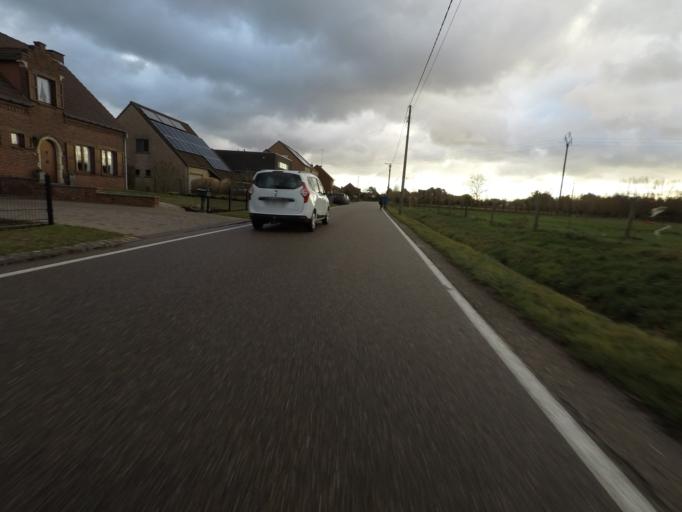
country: BE
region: Flanders
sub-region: Provincie Vlaams-Brabant
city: Begijnendijk
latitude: 51.0130
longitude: 4.7755
